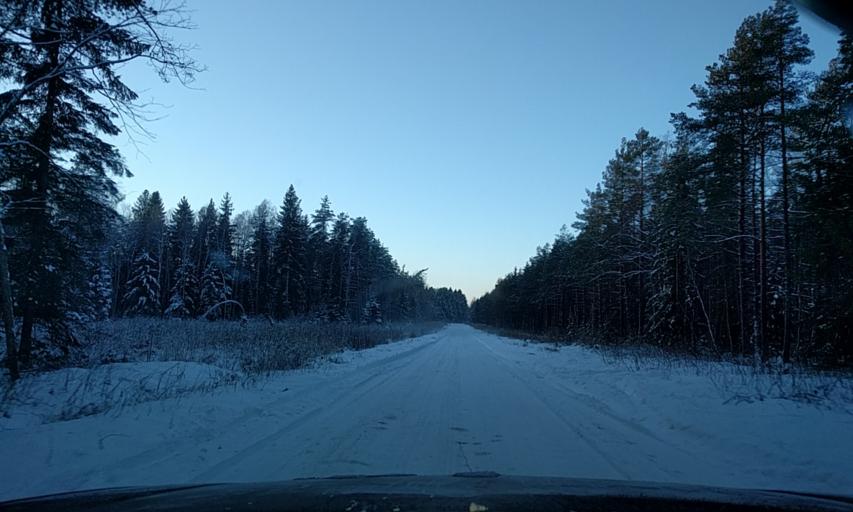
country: EE
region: Harju
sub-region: Saku vald
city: Saku
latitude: 59.3211
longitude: 24.6691
